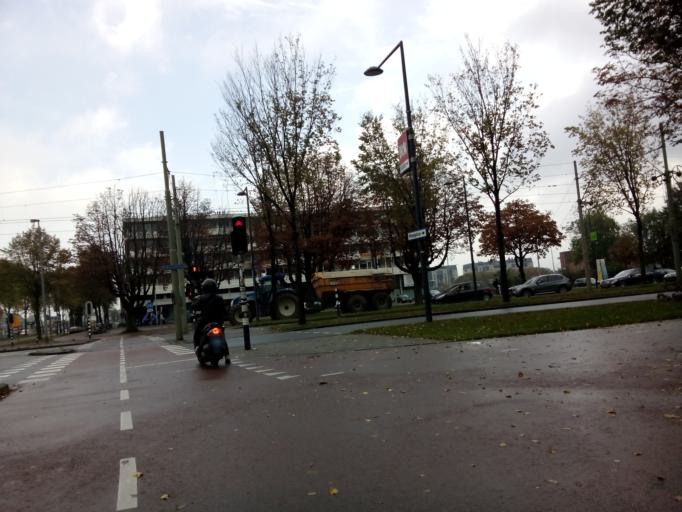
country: NL
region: South Holland
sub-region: Gemeente Delft
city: Delft
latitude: 52.0017
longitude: 4.3531
